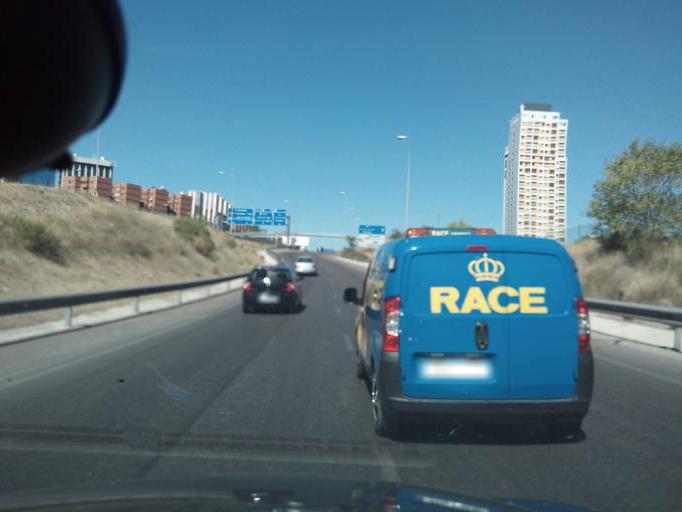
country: ES
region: Madrid
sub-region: Provincia de Madrid
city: Pinar de Chamartin
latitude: 40.4842
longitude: -3.6634
